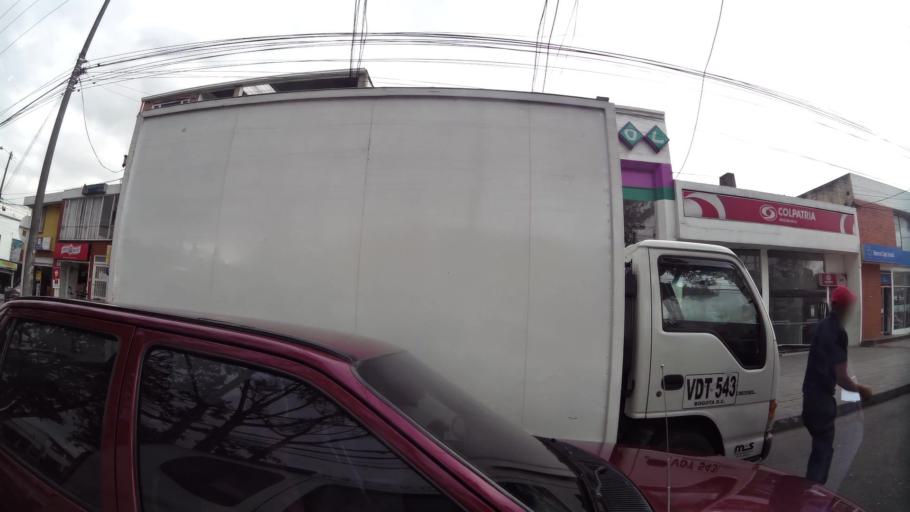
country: CO
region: Bogota D.C.
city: Bogota
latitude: 4.6655
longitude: -74.1205
